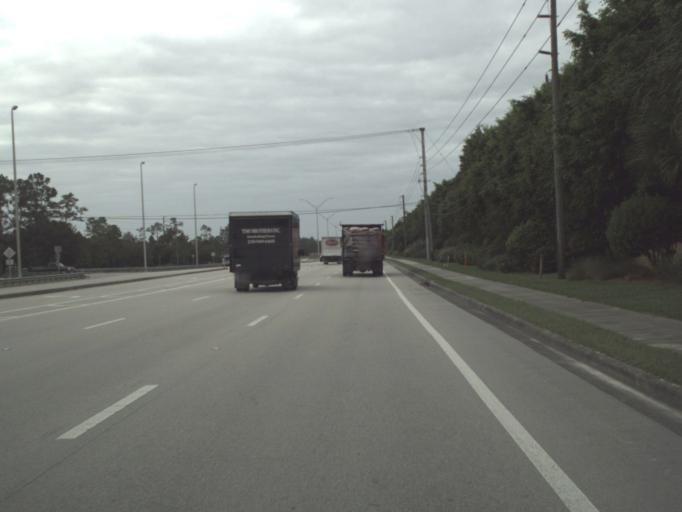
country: US
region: Florida
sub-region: Collier County
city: Lely Resort
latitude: 26.0963
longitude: -81.6874
